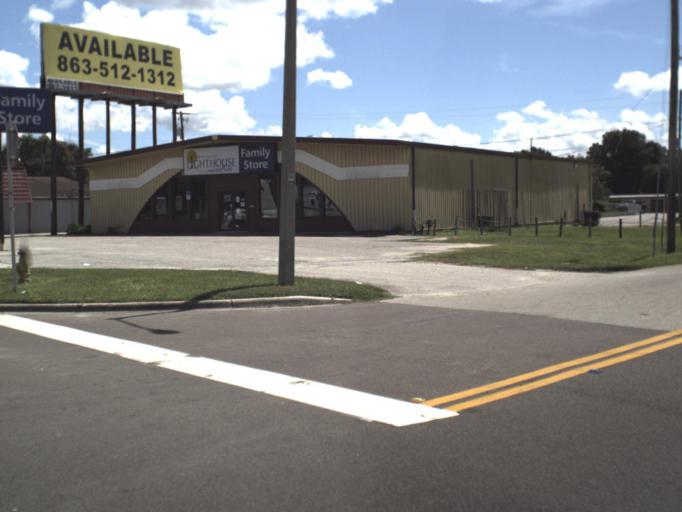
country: US
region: Florida
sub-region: Polk County
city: Inwood
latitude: 28.0481
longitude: -81.7644
